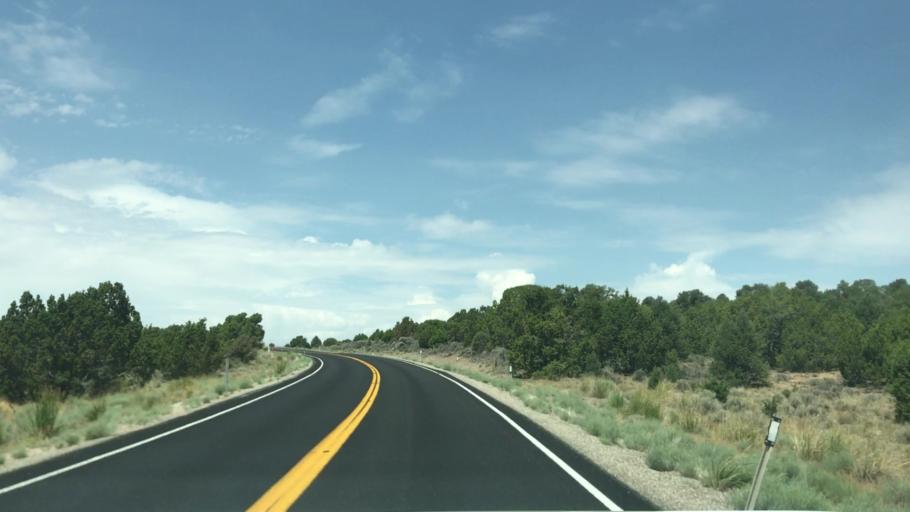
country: US
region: Nevada
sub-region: Eureka County
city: Eureka
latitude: 39.3963
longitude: -115.4640
